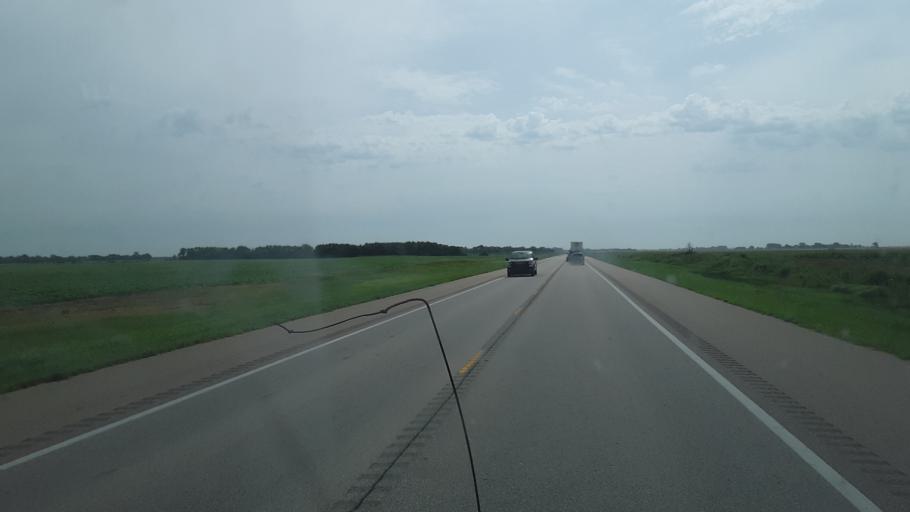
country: US
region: Kansas
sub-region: Reno County
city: Nickerson
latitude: 37.9850
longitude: -98.2221
